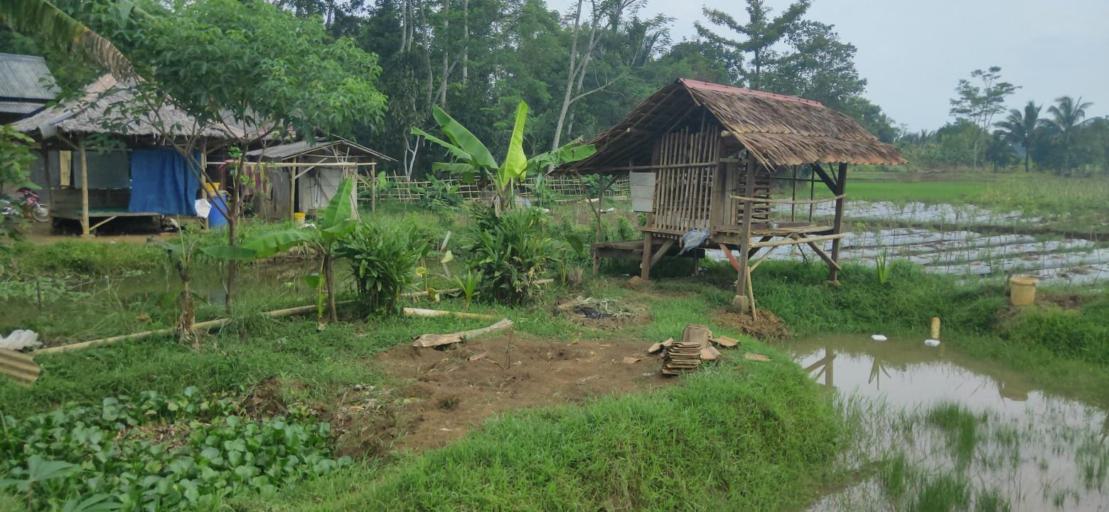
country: ID
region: West Java
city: Pangradin Satu
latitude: -6.4503
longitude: 106.4598
